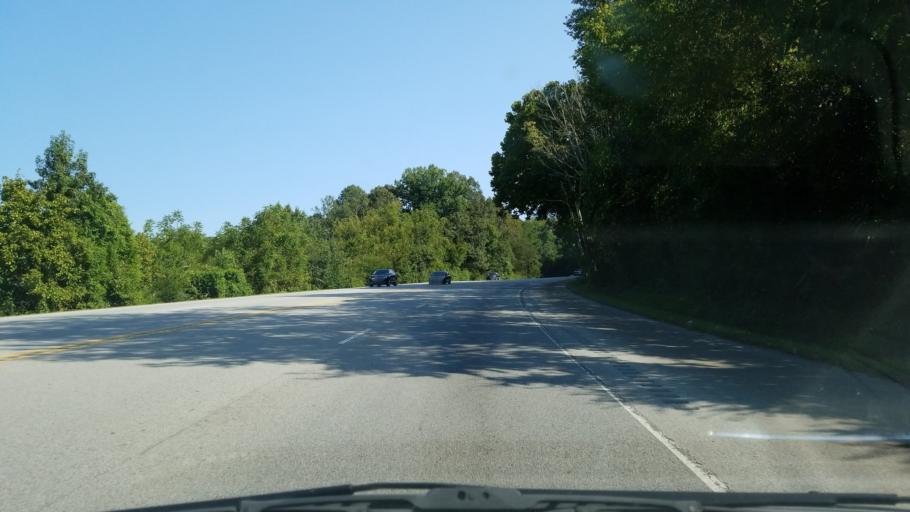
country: US
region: Tennessee
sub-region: Hamilton County
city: East Chattanooga
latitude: 35.0915
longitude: -85.2254
